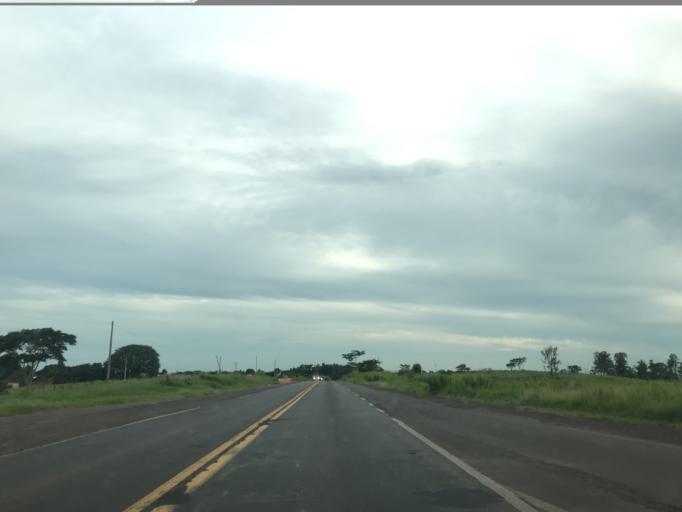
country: BR
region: Sao Paulo
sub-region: Tupa
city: Tupa
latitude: -21.6458
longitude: -50.5090
